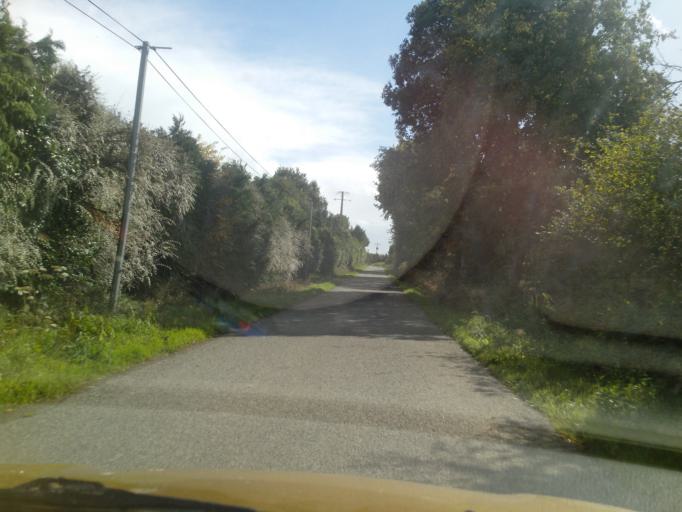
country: FR
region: Brittany
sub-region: Departement des Cotes-d'Armor
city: Merdrignac
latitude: 48.1505
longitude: -2.4134
